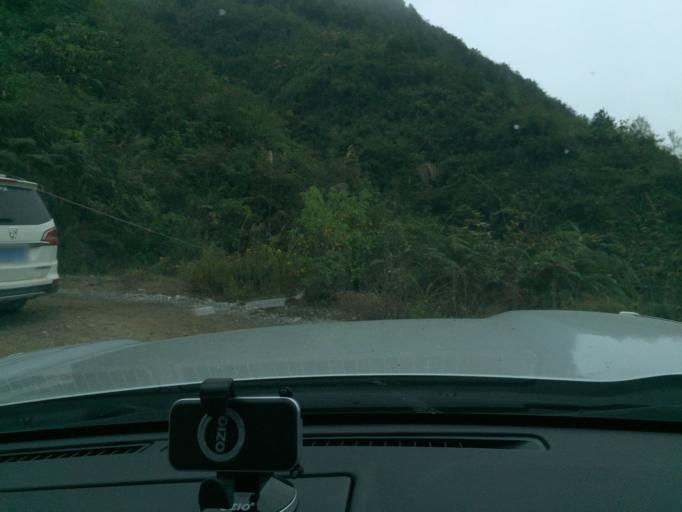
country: CN
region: Guizhou Sheng
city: Jiancha
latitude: 28.1718
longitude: 108.0047
